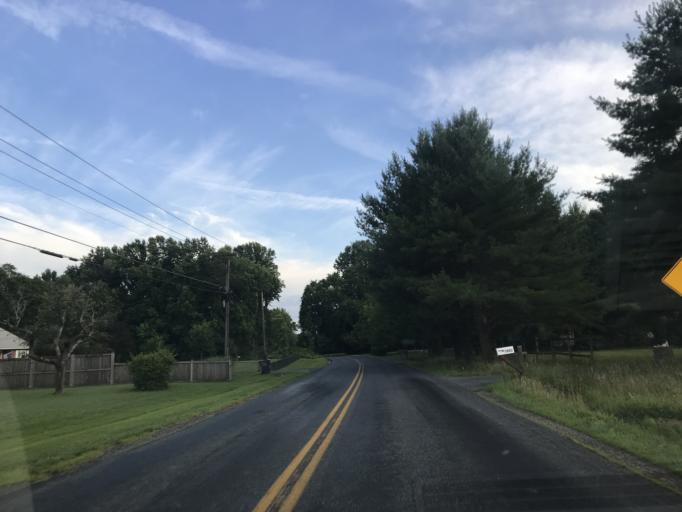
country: US
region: Maryland
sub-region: Harford County
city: Perryman
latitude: 39.5090
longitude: -76.2066
